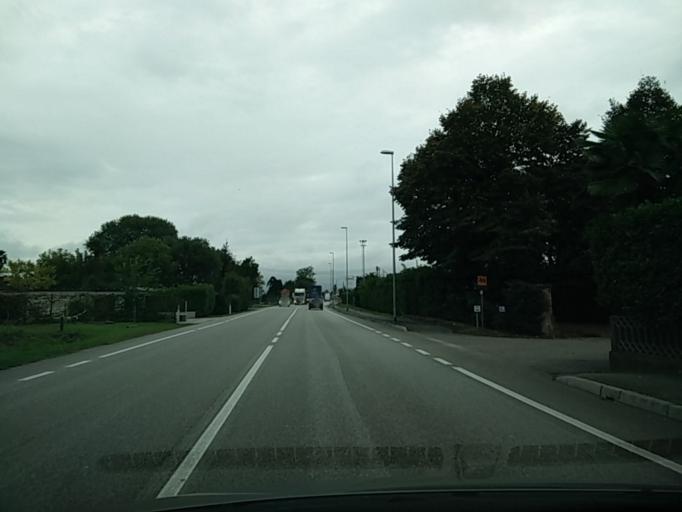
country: IT
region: Veneto
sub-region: Provincia di Padova
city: San Martino di Lupari
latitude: 45.6678
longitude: 11.8650
